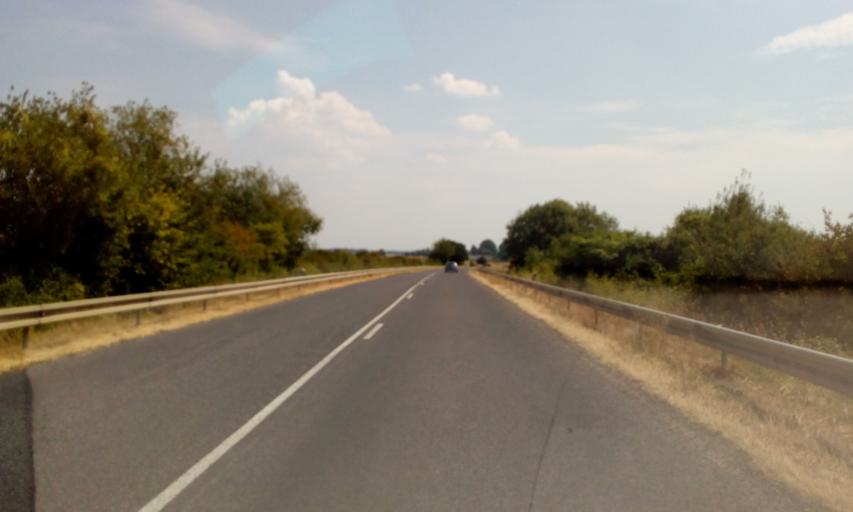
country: FR
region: Lorraine
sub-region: Departement de la Meuse
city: Etain
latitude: 49.1151
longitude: 5.5810
